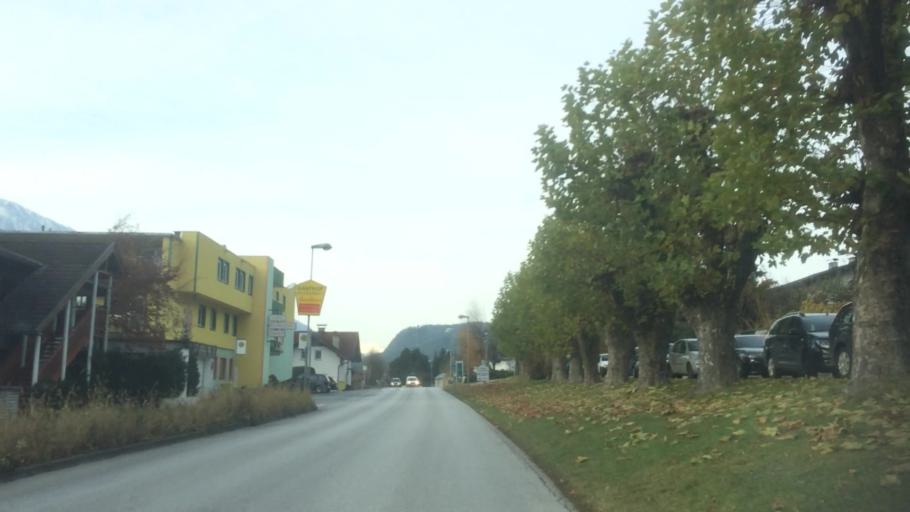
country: AT
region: Tyrol
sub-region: Politischer Bezirk Innsbruck Land
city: Pfaffenhofen
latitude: 47.3138
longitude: 11.0818
